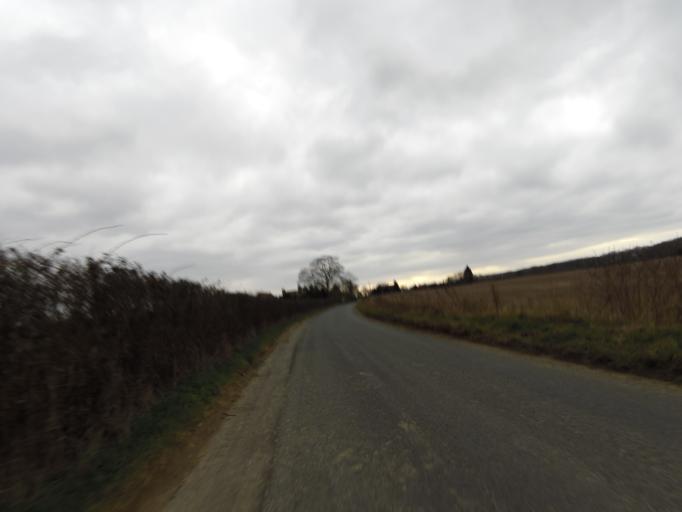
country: GB
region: England
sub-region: Suffolk
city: Ipswich
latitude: 52.1286
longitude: 1.1489
